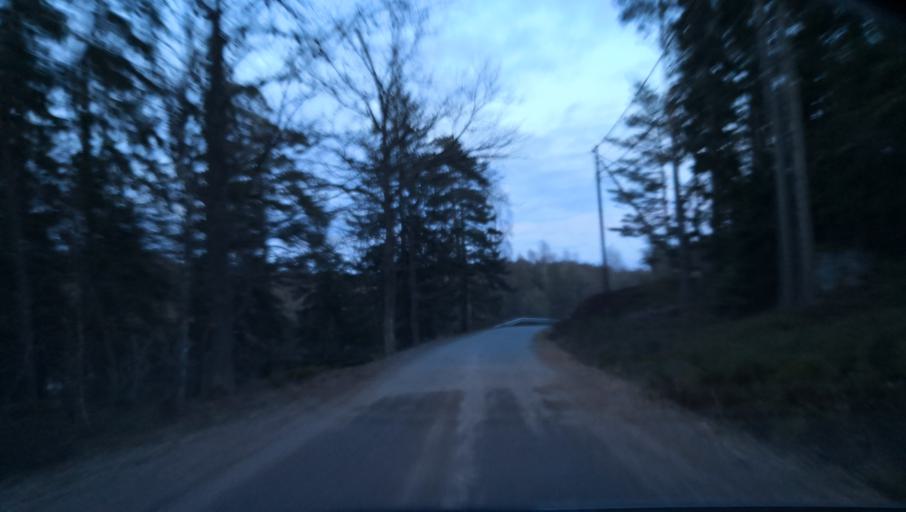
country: SE
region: Stockholm
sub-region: Nacka Kommun
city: Boo
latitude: 59.3279
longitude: 18.3253
